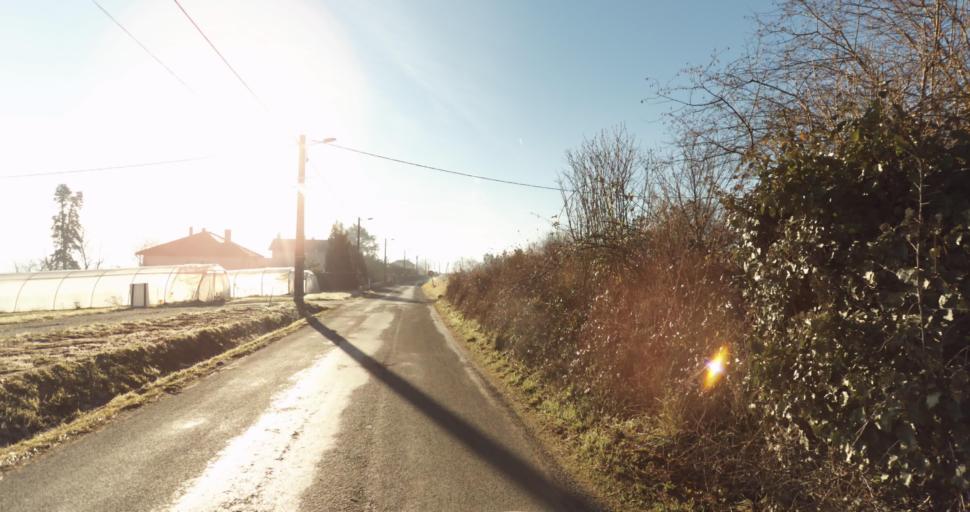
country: FR
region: Limousin
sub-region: Departement de la Haute-Vienne
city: Aixe-sur-Vienne
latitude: 45.8039
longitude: 1.1453
